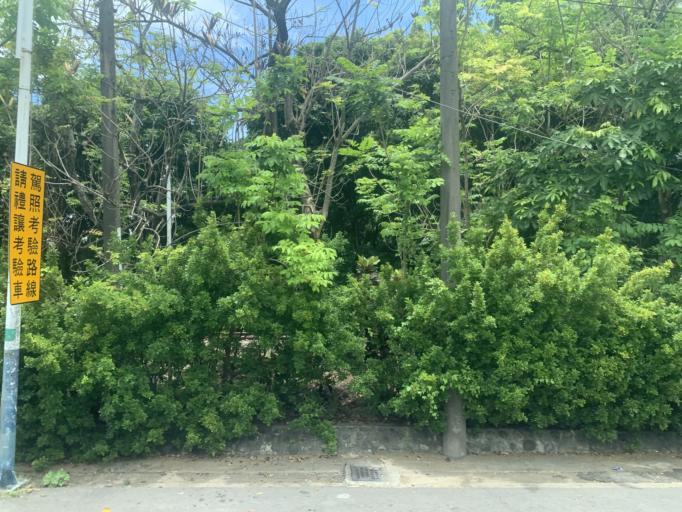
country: TW
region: Taiwan
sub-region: Chiayi
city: Jiayi Shi
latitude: 23.4917
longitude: 120.4698
